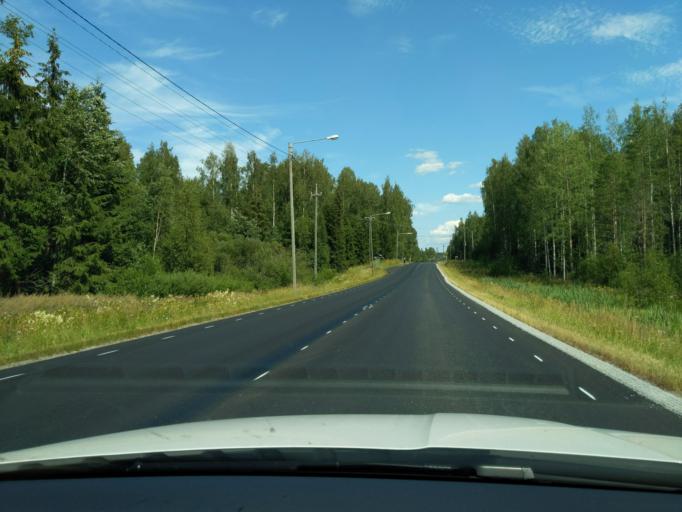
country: FI
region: Paijanne Tavastia
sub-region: Lahti
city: Lahti
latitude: 61.0356
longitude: 25.7469
